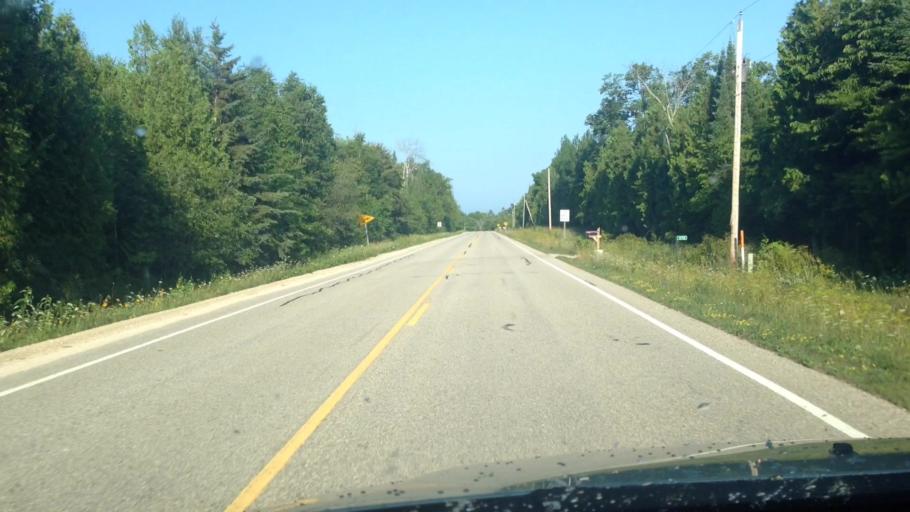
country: US
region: Michigan
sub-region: Mackinac County
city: Saint Ignace
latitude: 45.8938
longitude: -84.8157
